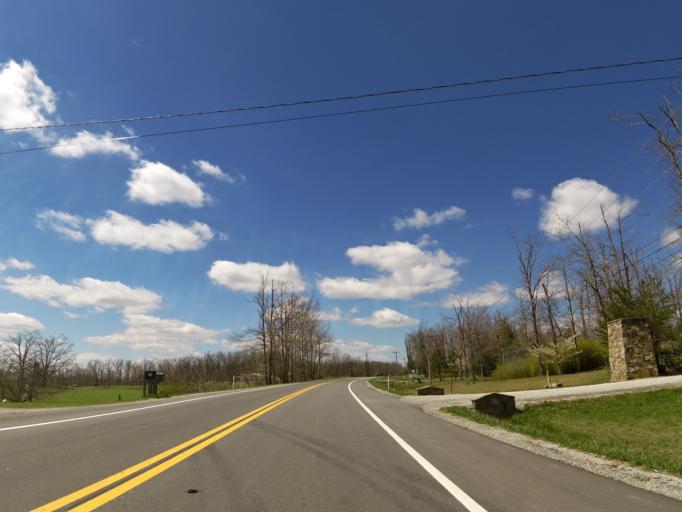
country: US
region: Tennessee
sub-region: Putnam County
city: Monterey
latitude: 35.9643
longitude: -85.2418
